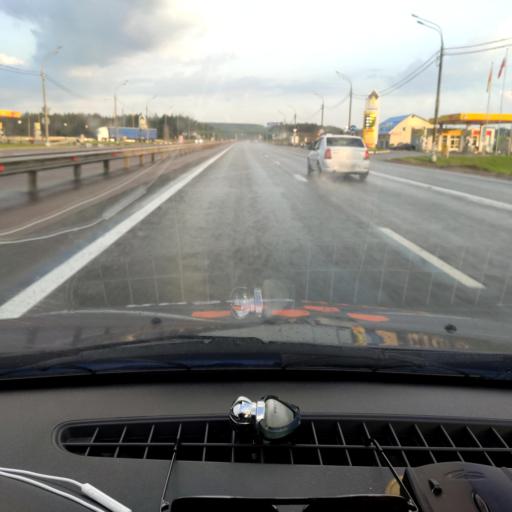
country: RU
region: Lipetsk
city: Zadonsk
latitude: 52.3753
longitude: 38.8956
